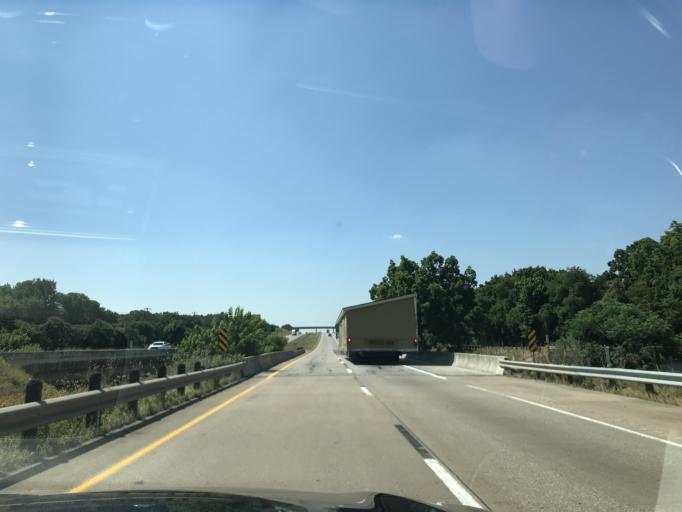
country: US
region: Texas
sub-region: Johnson County
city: Alvarado
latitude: 32.3861
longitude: -97.2077
